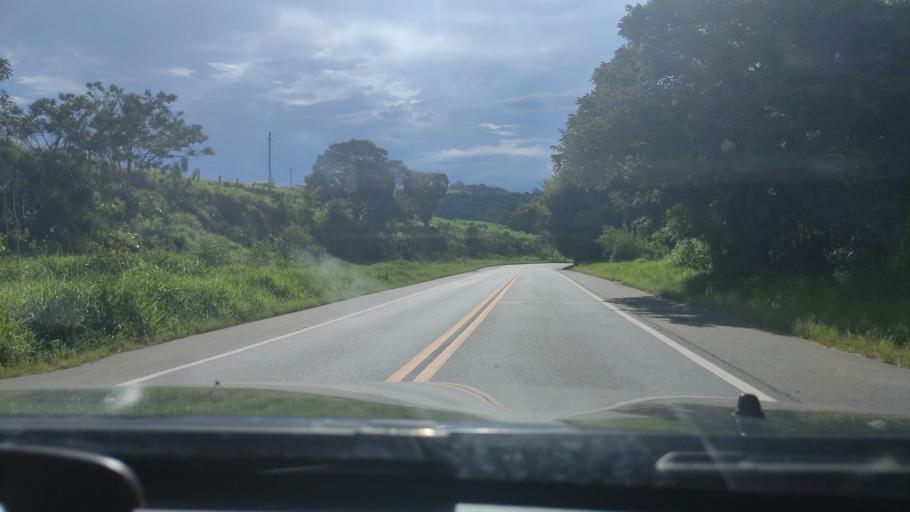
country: BR
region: Sao Paulo
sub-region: Aguas De Lindoia
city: Aguas de Lindoia
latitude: -22.5365
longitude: -46.6316
